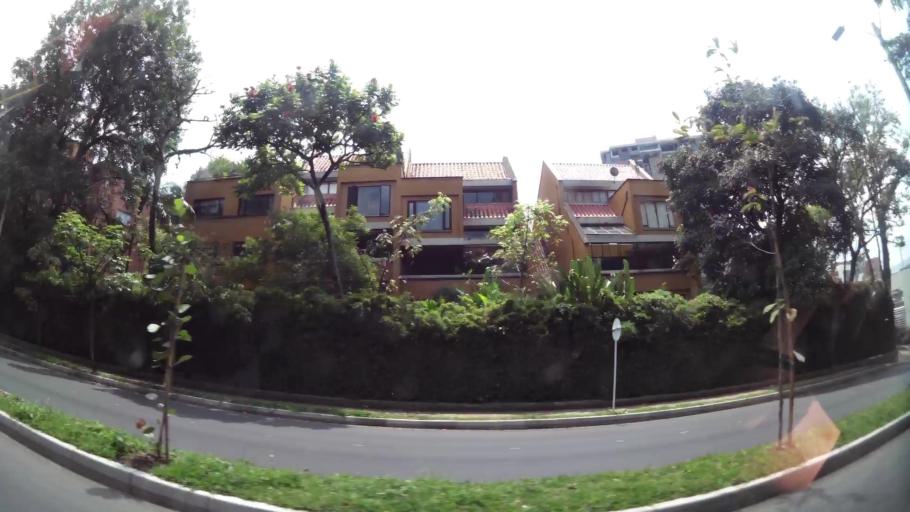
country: CO
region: Antioquia
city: Envigado
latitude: 6.1830
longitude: -75.5784
